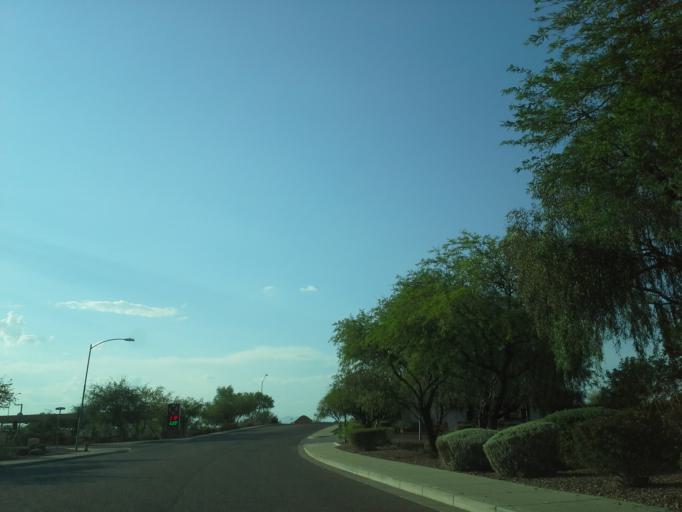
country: US
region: Arizona
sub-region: Maricopa County
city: Anthem
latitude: 33.8696
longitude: -112.1488
